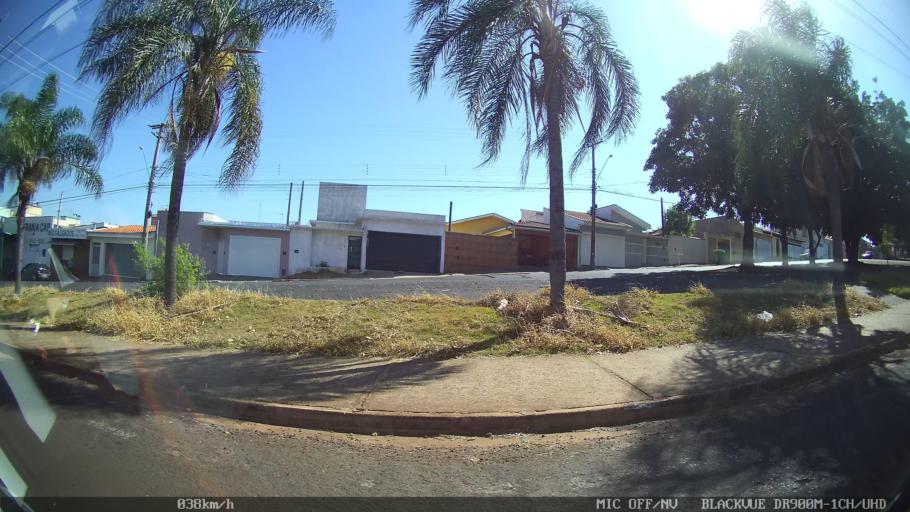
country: BR
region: Sao Paulo
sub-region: Batatais
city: Batatais
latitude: -20.8874
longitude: -47.5758
